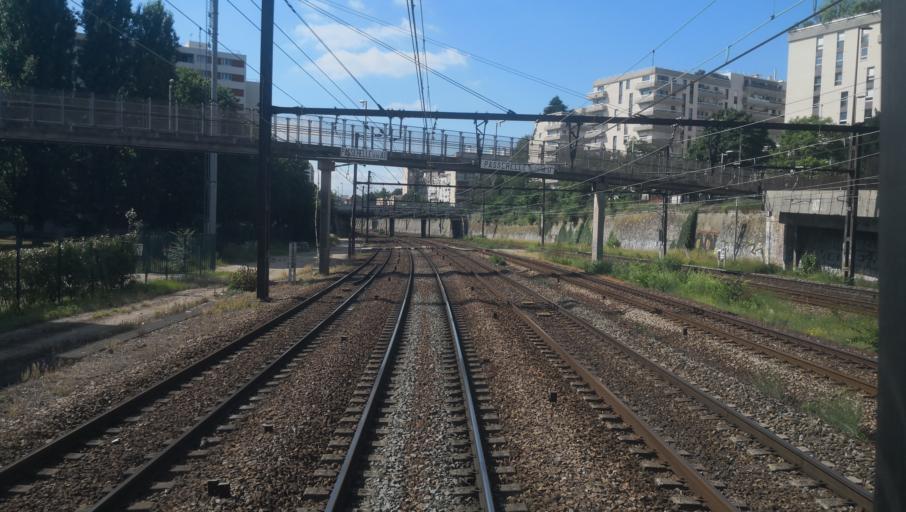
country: FR
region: Ile-de-France
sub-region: Departement du Val-de-Marne
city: Charenton-le-Pont
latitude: 48.8190
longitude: 2.4139
